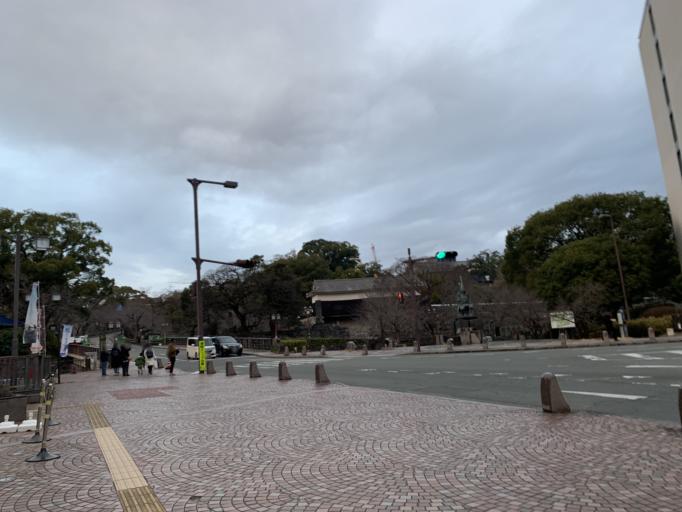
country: JP
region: Kumamoto
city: Kumamoto
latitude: 32.8022
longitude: 130.7050
